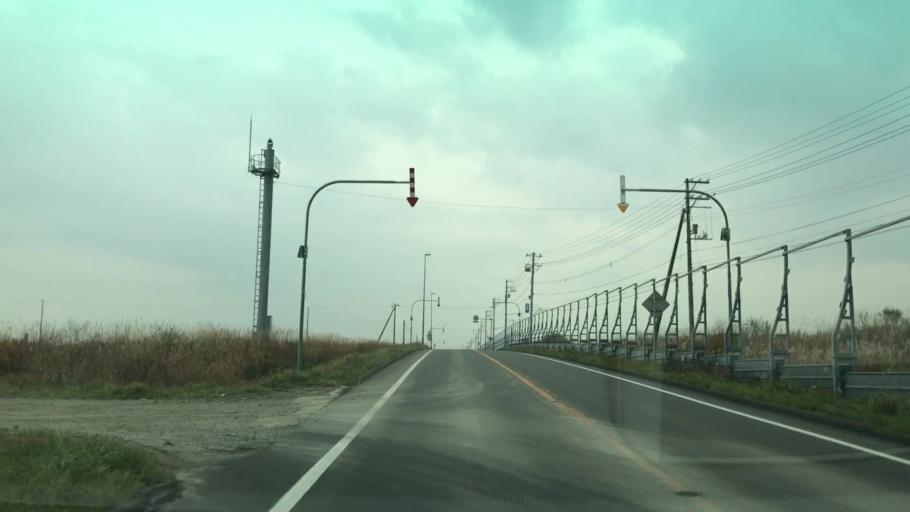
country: JP
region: Hokkaido
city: Ishikari
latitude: 43.3015
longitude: 141.4122
